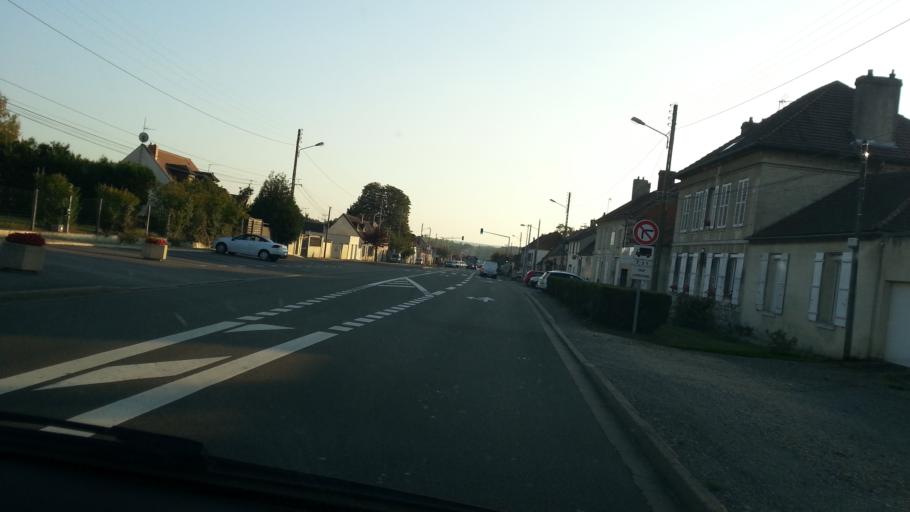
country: FR
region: Picardie
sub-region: Departement de l'Oise
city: Saint-Martin-Longueau
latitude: 49.3436
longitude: 2.6068
